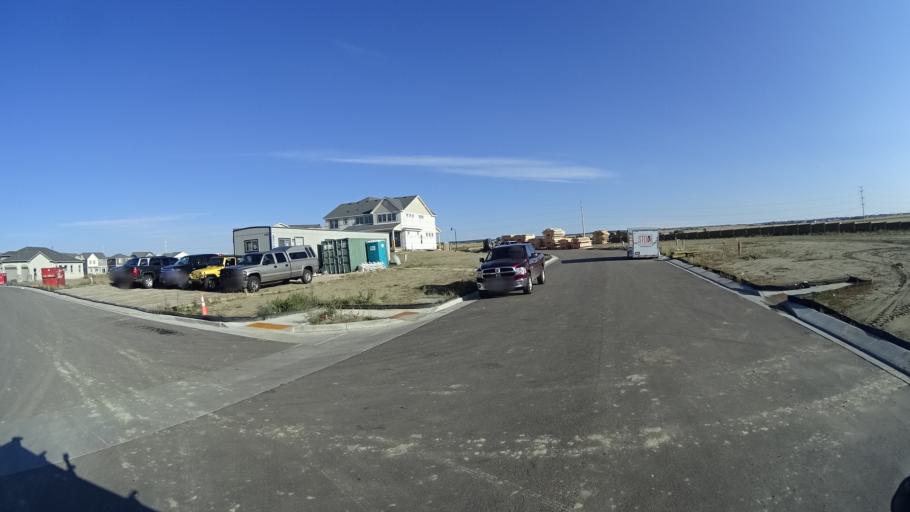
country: US
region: Colorado
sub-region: El Paso County
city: Cimarron Hills
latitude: 38.9347
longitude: -104.6526
